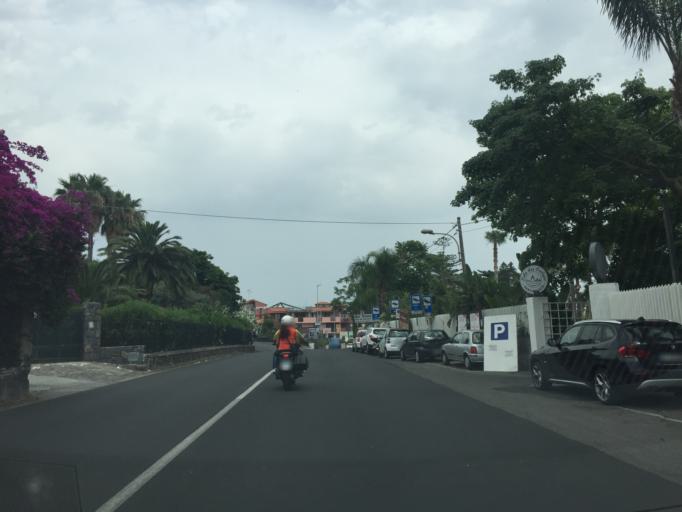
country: IT
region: Sicily
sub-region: Catania
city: Acitrezza
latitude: 37.5602
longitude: 15.1557
